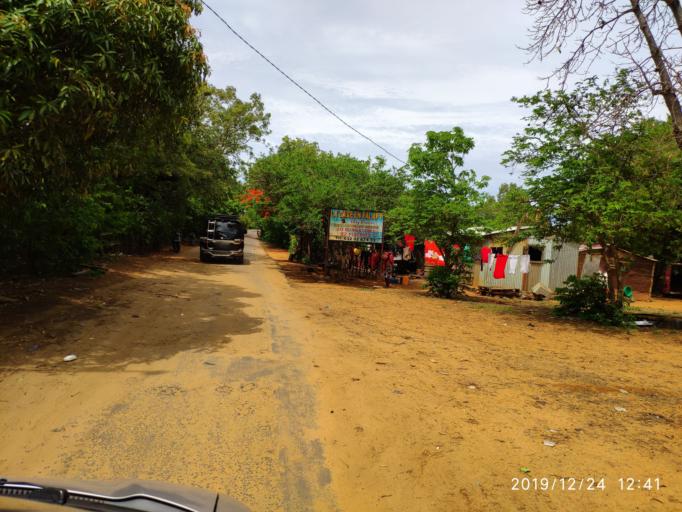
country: MG
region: Diana
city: Antsiranana
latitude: -12.2837
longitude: 49.3591
